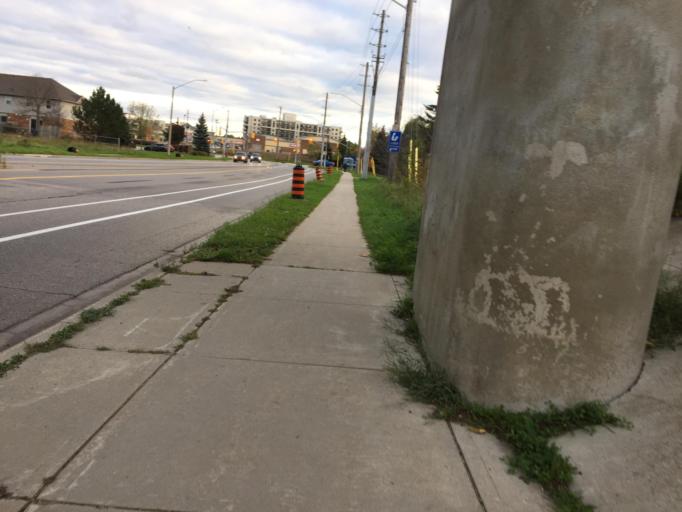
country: CA
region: Ontario
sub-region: Wellington County
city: Guelph
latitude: 43.5264
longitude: -80.2898
